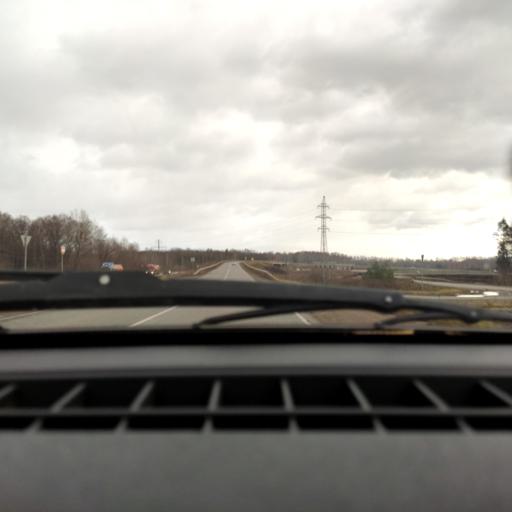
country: RU
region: Bashkortostan
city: Iglino
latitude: 54.7455
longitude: 56.2993
